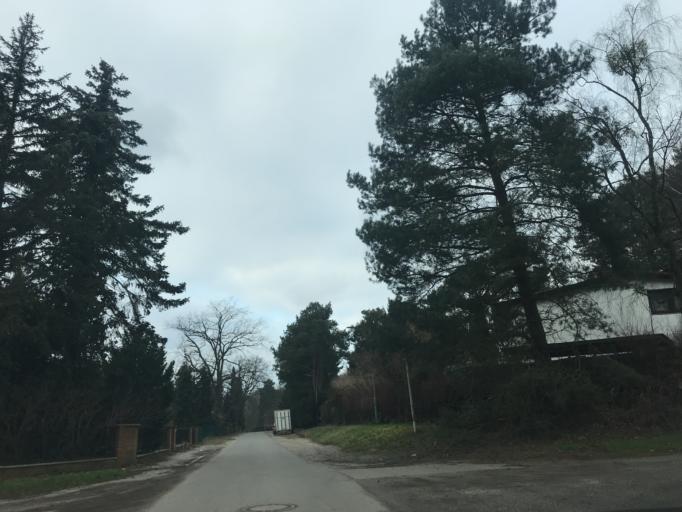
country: DE
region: Berlin
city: Kladow
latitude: 52.4548
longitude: 13.1210
